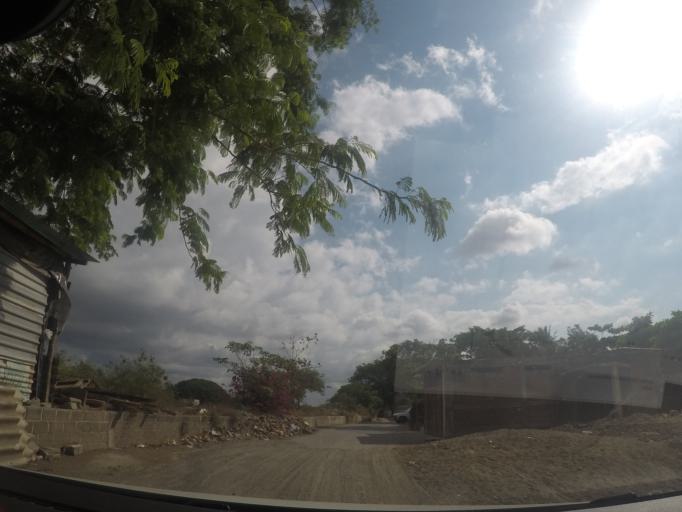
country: MX
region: Oaxaca
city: Juchitan de Zaragoza
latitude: 16.4288
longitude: -95.0263
